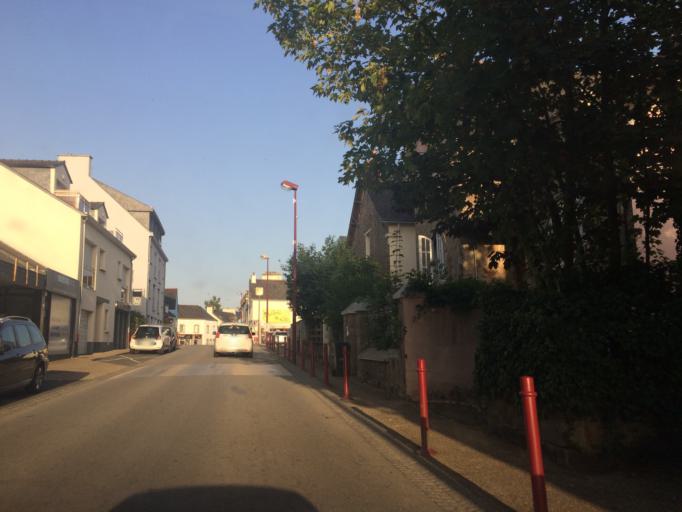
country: FR
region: Brittany
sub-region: Departement du Morbihan
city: Muzillac
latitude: 47.5531
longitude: -2.4838
